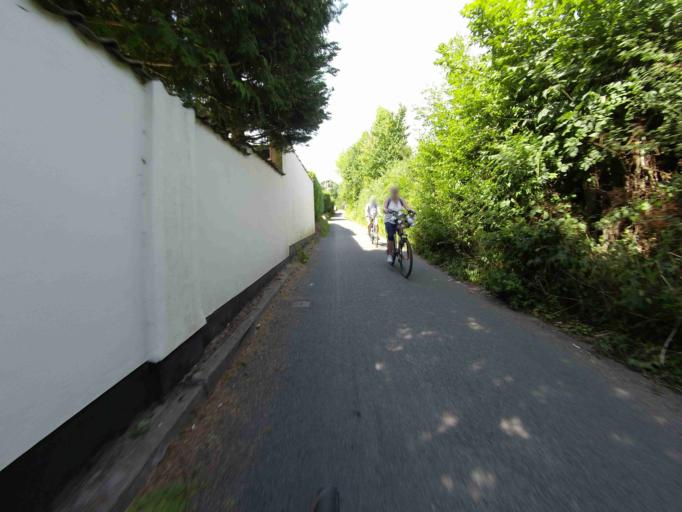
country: GB
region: England
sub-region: Devon
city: Topsham
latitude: 50.6691
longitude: -3.4411
